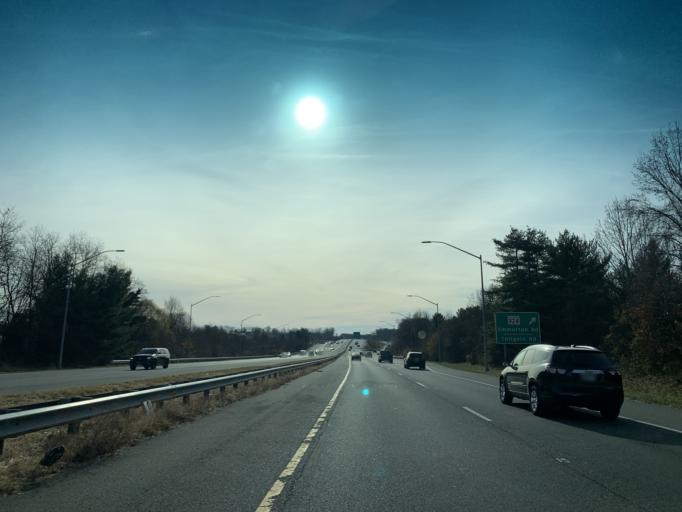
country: US
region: Maryland
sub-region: Harford County
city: Bel Air South
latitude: 39.4703
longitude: -76.3169
